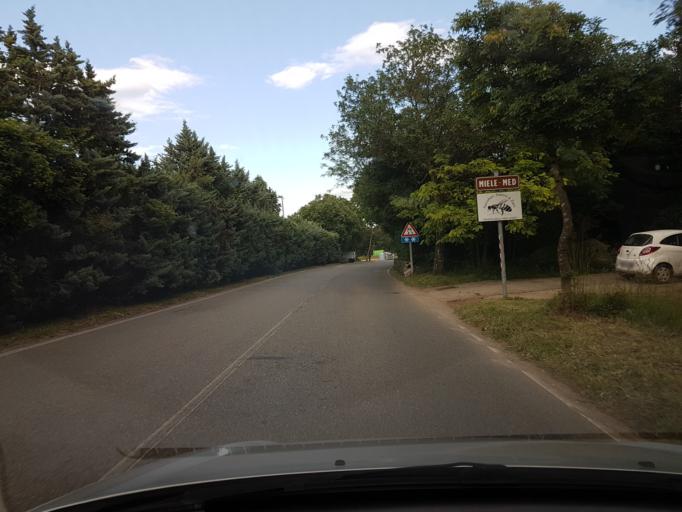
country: IT
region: Friuli Venezia Giulia
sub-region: Provincia di Trieste
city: Villa Opicina
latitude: 45.6772
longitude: 13.8160
